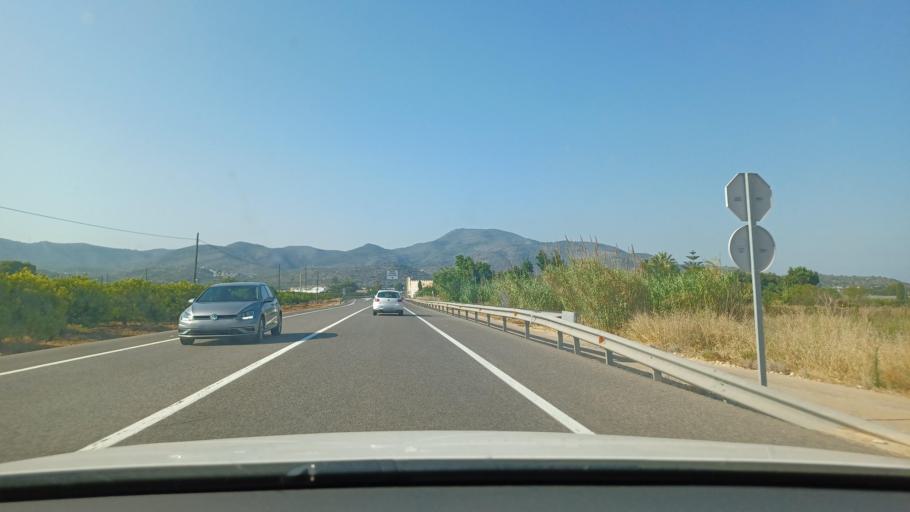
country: ES
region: Catalonia
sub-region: Provincia de Tarragona
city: Alcanar
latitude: 40.5424
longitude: 0.5080
